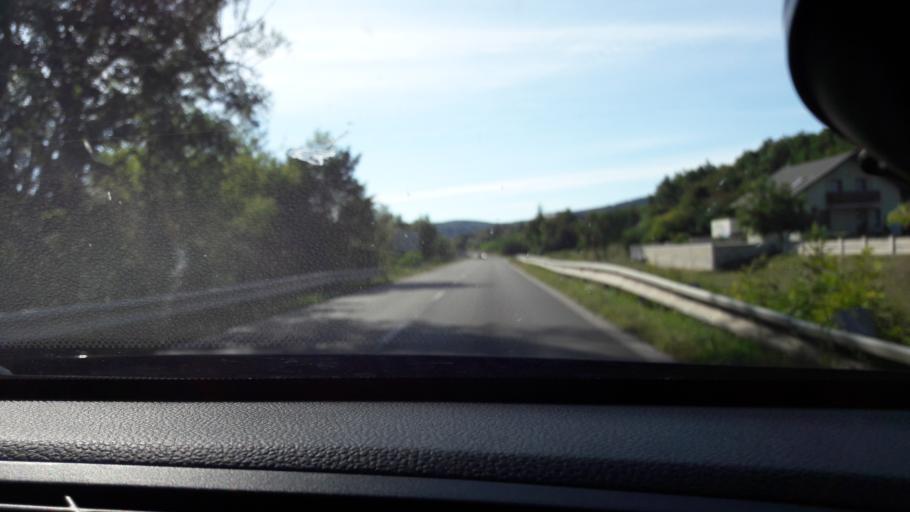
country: SK
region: Kosicky
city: Vinne
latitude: 48.8099
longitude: 22.0256
